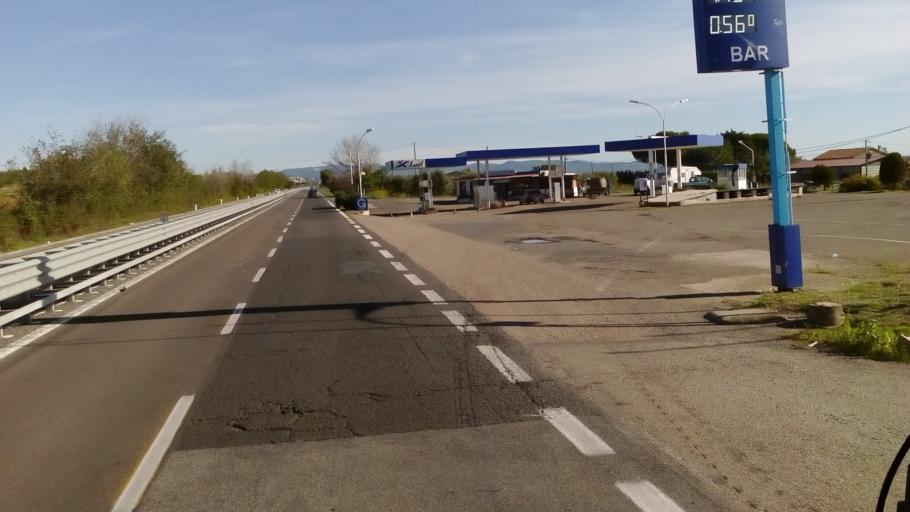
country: IT
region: Latium
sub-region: Provincia di Viterbo
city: Tarquinia
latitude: 42.2739
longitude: 11.7085
